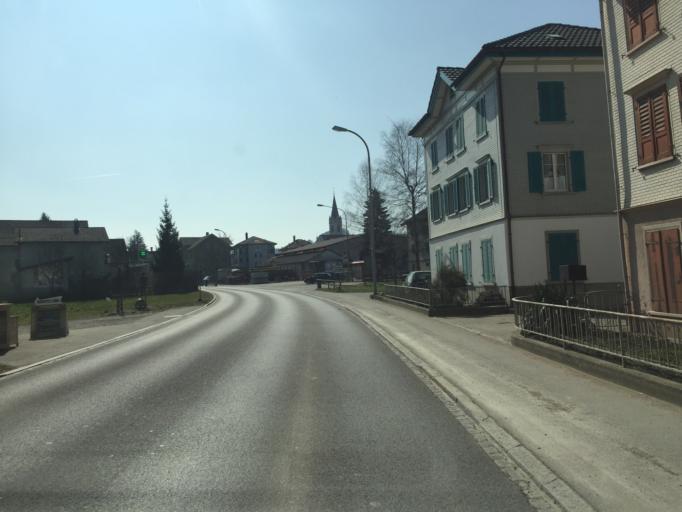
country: CH
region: Saint Gallen
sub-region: Wahlkreis Toggenburg
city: Buetschwil
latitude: 47.3641
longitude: 9.0733
